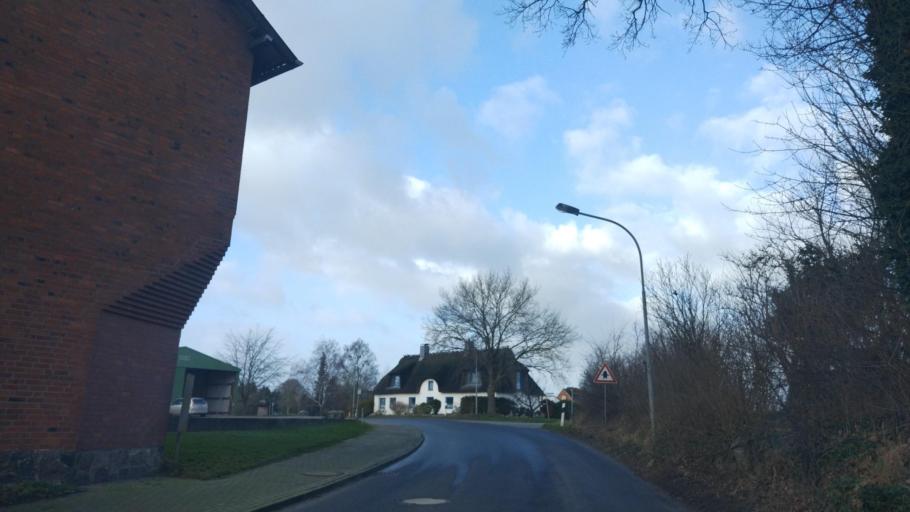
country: DE
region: Schleswig-Holstein
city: Taarstedt
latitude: 54.5661
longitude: 9.6765
